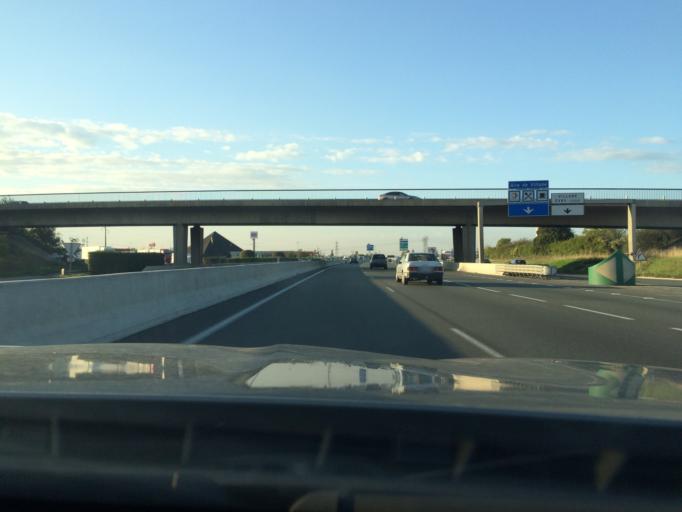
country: FR
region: Ile-de-France
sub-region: Departement de l'Essonne
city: Villabe
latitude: 48.5917
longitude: 2.4452
